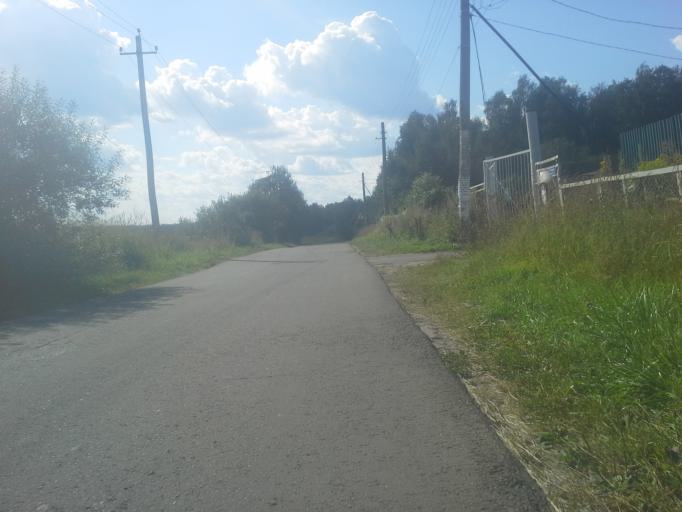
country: RU
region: Moskovskaya
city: Kievskij
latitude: 55.3287
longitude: 37.0120
